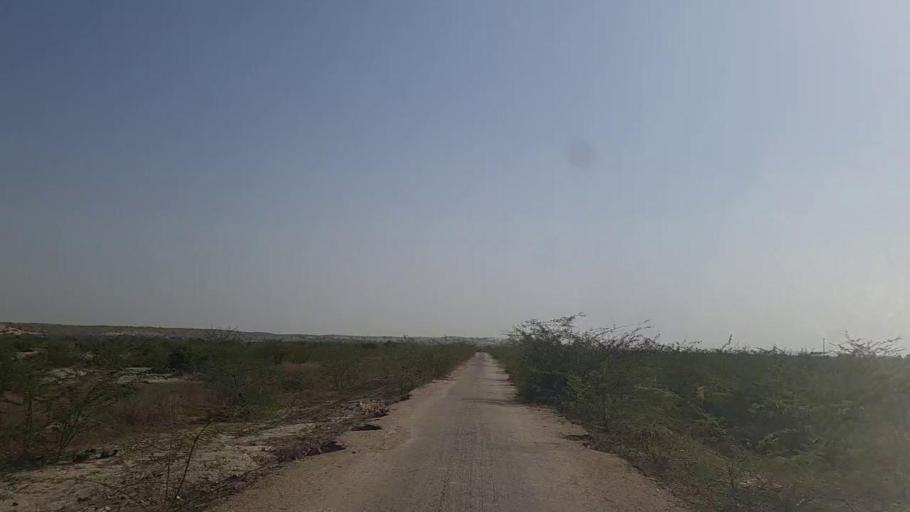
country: PK
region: Sindh
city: Naukot
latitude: 24.5908
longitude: 69.2924
